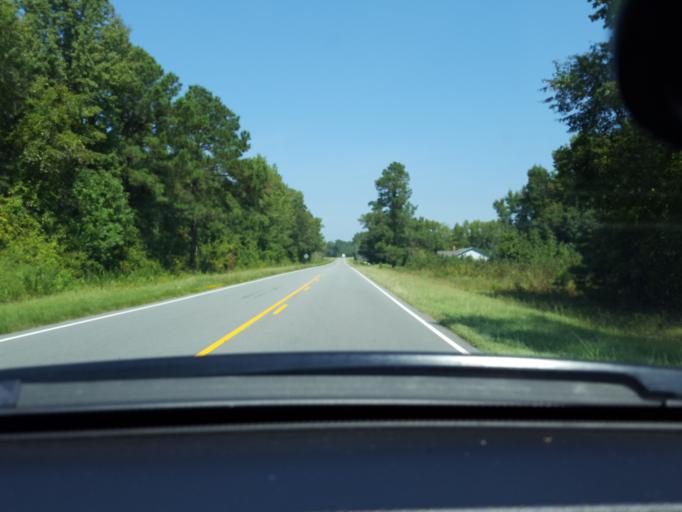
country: US
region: North Carolina
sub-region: Bladen County
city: Elizabethtown
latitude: 34.6733
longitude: -78.4901
